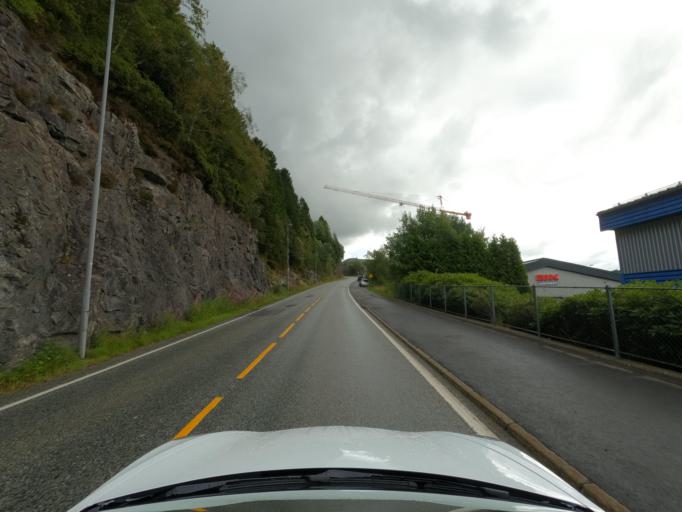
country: NO
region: Hordaland
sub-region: Bergen
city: Hylkje
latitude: 60.4727
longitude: 5.3436
